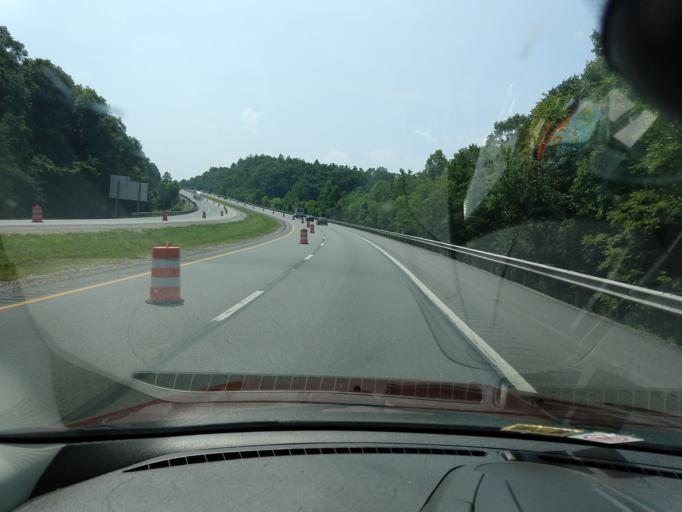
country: US
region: West Virginia
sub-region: Jackson County
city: Ripley
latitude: 38.7954
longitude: -81.7332
